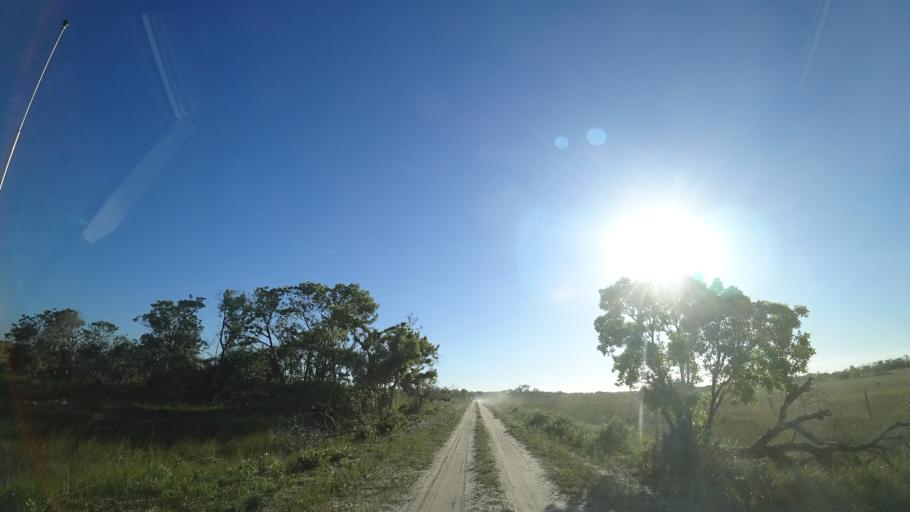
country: MZ
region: Sofala
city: Beira
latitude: -19.5758
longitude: 35.2070
